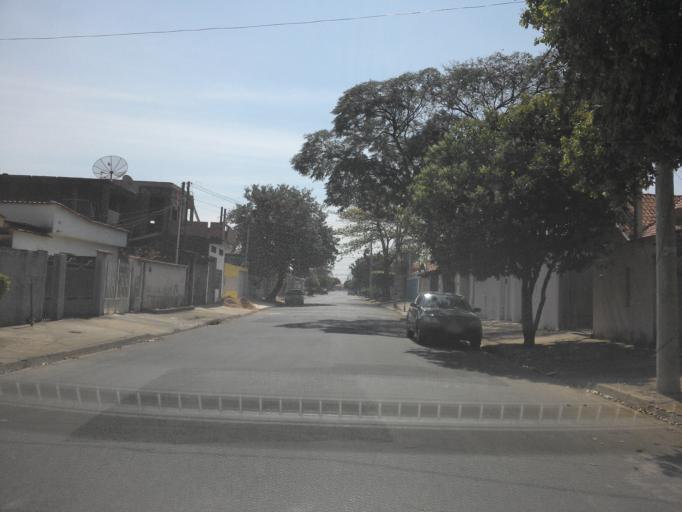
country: BR
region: Sao Paulo
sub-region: Hortolandia
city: Hortolandia
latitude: -22.8894
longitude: -47.2315
